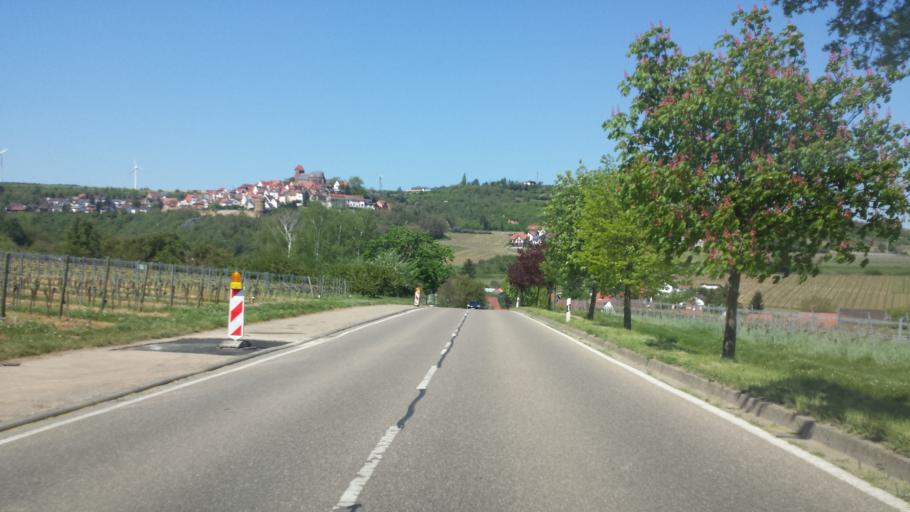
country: DE
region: Rheinland-Pfalz
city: Kleinkarlbach
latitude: 49.5376
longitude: 8.1504
